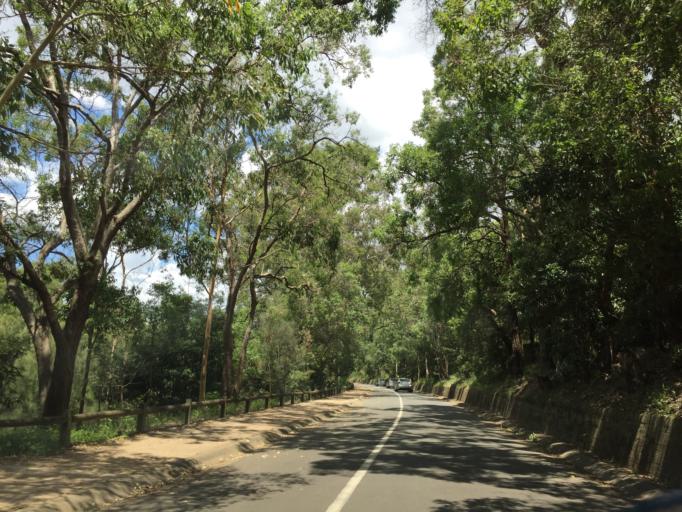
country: AU
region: New South Wales
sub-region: Parramatta
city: City of Parramatta
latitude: -33.8072
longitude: 150.9967
